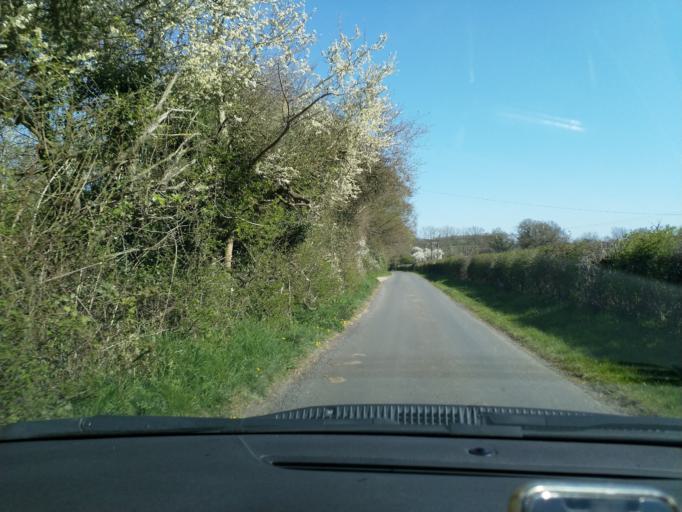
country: GB
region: England
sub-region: Warwickshire
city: Wroxall
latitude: 52.2909
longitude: -1.6829
